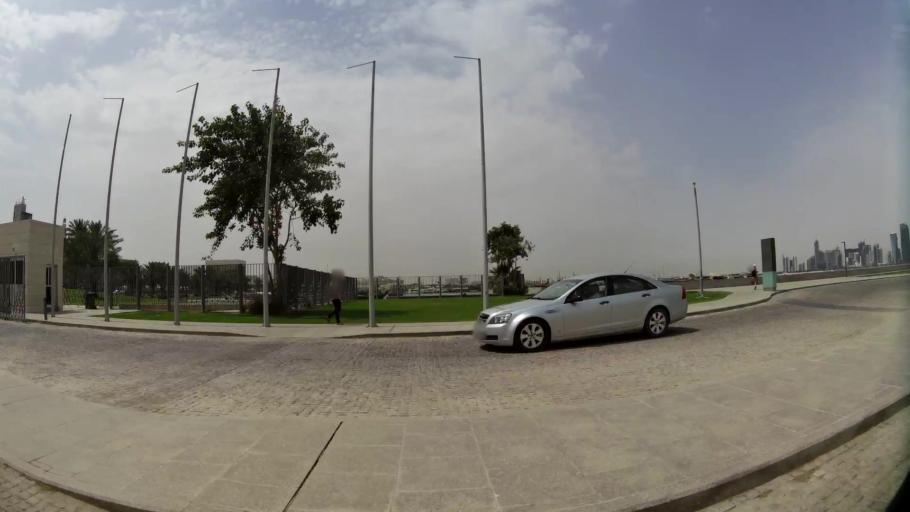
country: QA
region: Baladiyat ad Dawhah
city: Doha
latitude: 25.2922
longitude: 51.5393
